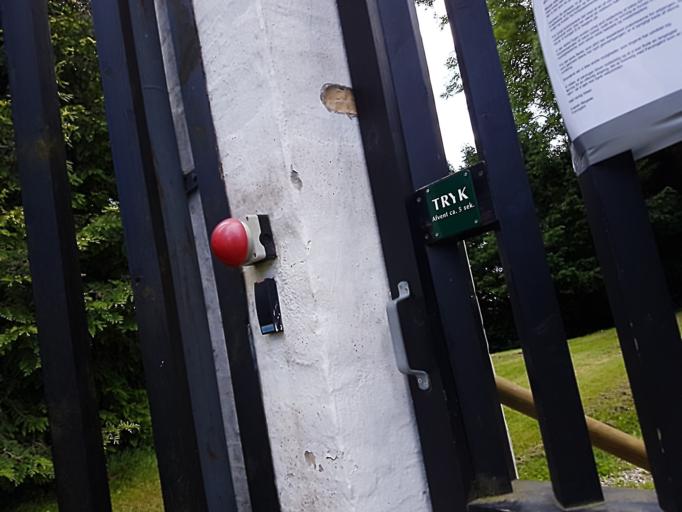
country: DK
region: Capital Region
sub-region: Fureso Kommune
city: Farum
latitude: 55.8067
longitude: 12.3598
